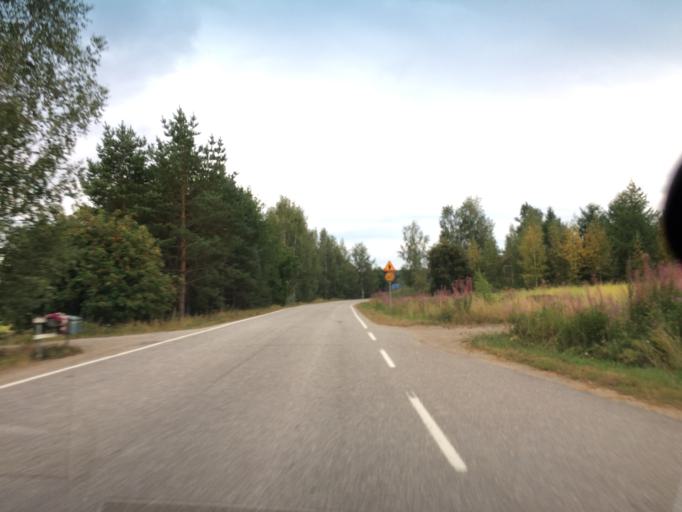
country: FI
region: Pirkanmaa
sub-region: Tampere
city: Luopioinen
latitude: 61.2597
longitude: 24.7115
